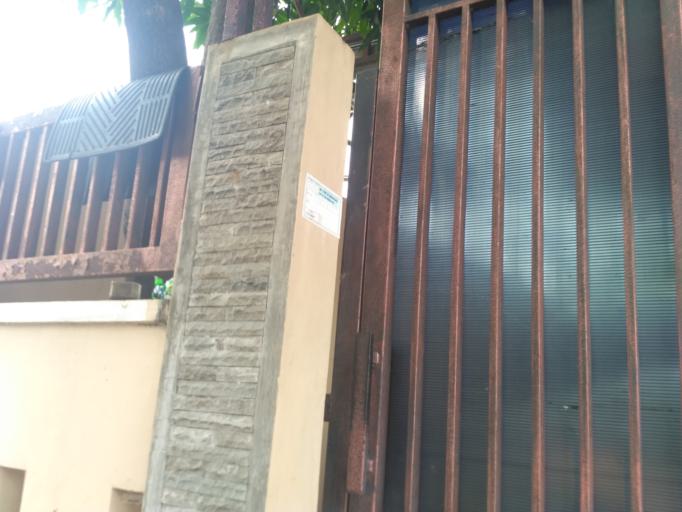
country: ID
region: Central Java
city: Mranggen
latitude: -7.0623
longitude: 110.4667
